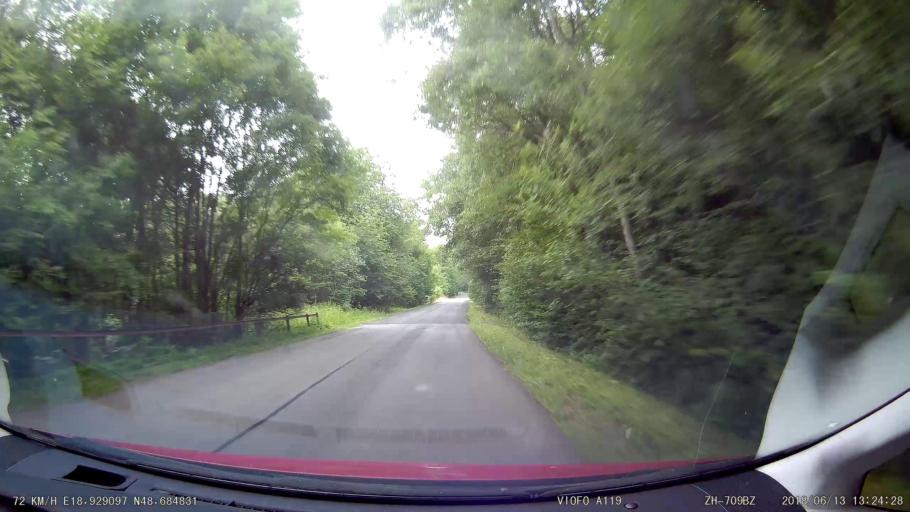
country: SK
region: Banskobystricky
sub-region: Okres Ziar nad Hronom
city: Kremnica
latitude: 48.6849
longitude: 18.9291
